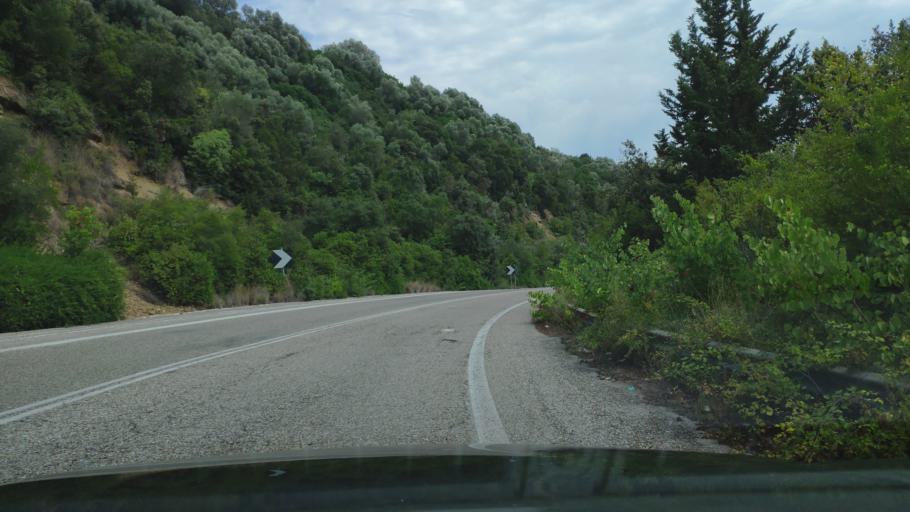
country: GR
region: West Greece
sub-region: Nomos Aitolias kai Akarnanias
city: Menidi
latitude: 39.0060
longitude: 21.1468
